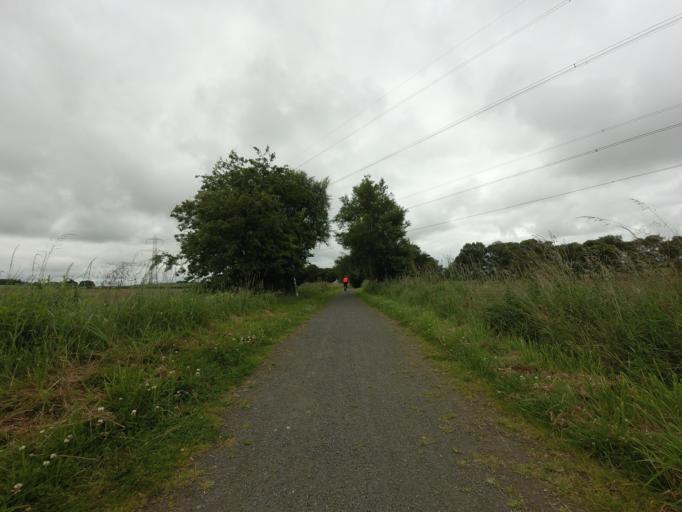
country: GB
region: Scotland
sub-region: Aberdeenshire
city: Mintlaw
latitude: 57.4927
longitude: -2.1359
